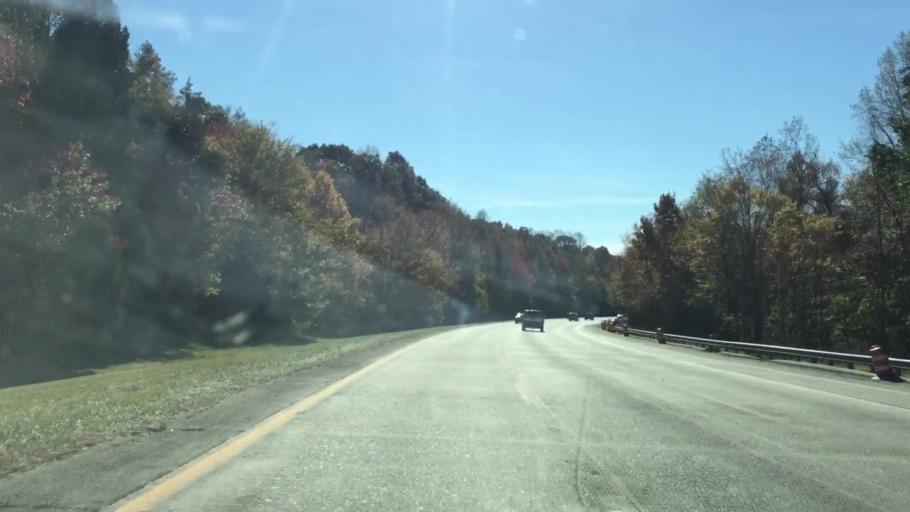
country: US
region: North Carolina
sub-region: Davidson County
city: Thomasville
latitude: 35.8386
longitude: -80.1322
